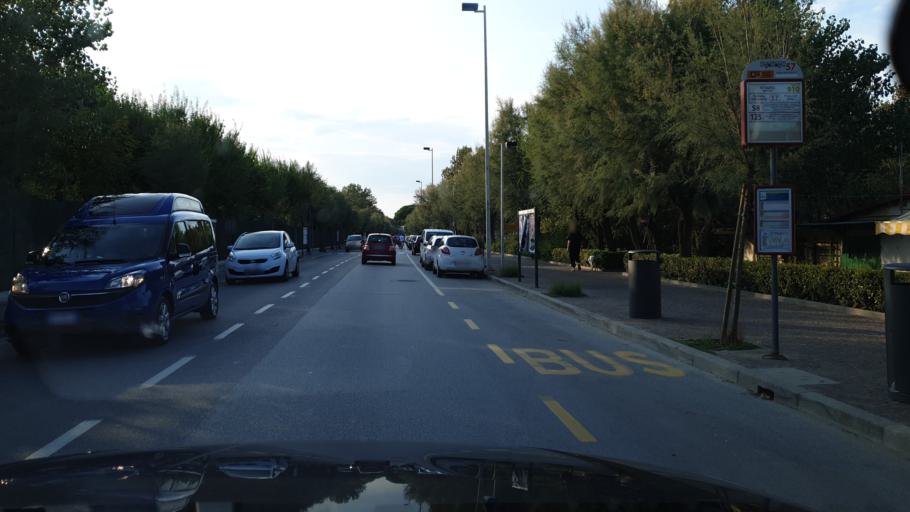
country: IT
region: Emilia-Romagna
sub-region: Provincia di Rimini
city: Riccione
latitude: 43.9913
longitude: 12.6787
